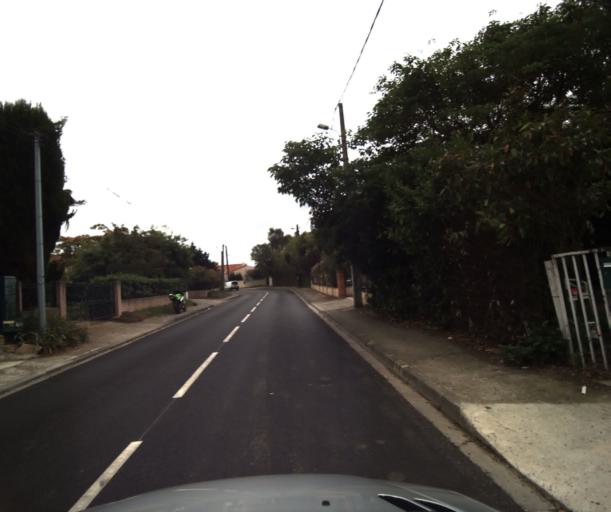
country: FR
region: Midi-Pyrenees
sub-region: Departement de la Haute-Garonne
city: Labarthe-sur-Leze
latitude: 43.4581
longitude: 1.4008
